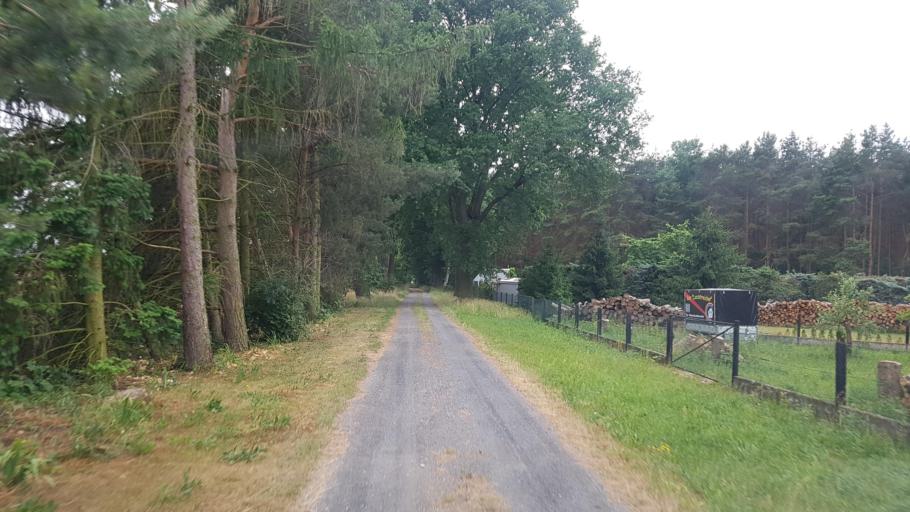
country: DE
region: Brandenburg
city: Schraden
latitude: 51.4221
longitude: 13.6880
